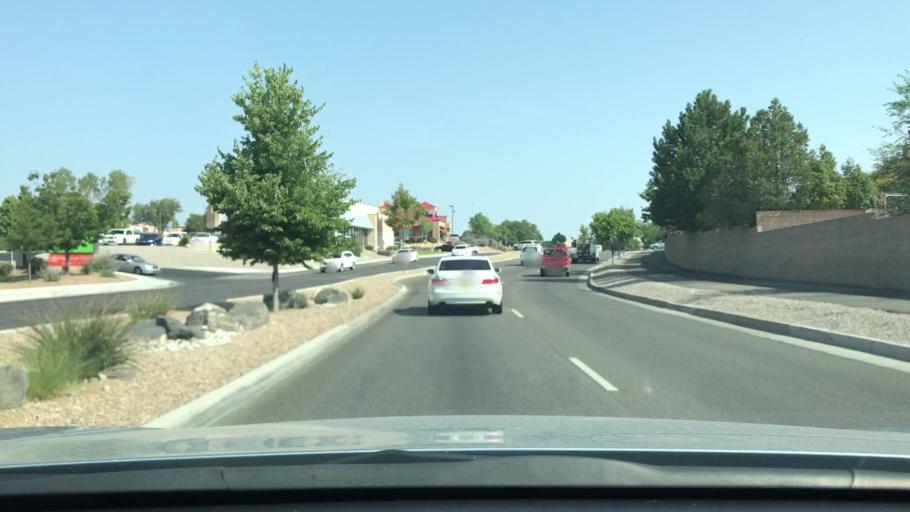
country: US
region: New Mexico
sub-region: Bernalillo County
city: Paradise Hills
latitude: 35.1804
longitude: -106.6877
